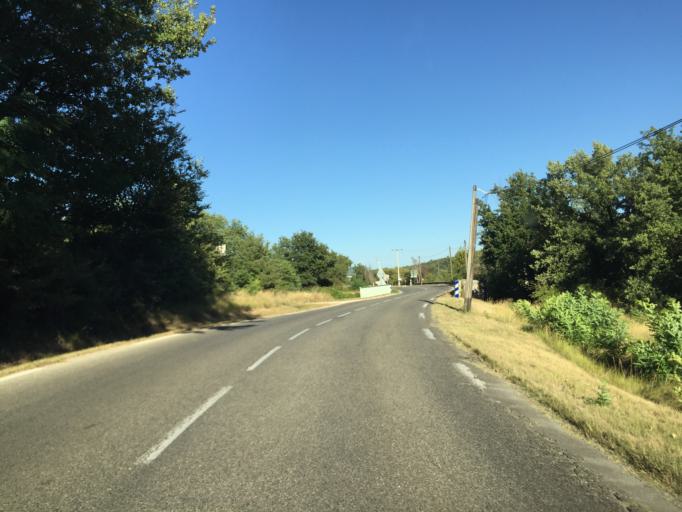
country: FR
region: Provence-Alpes-Cote d'Azur
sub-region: Departement du Vaucluse
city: Saignon
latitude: 43.8506
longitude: 5.4930
